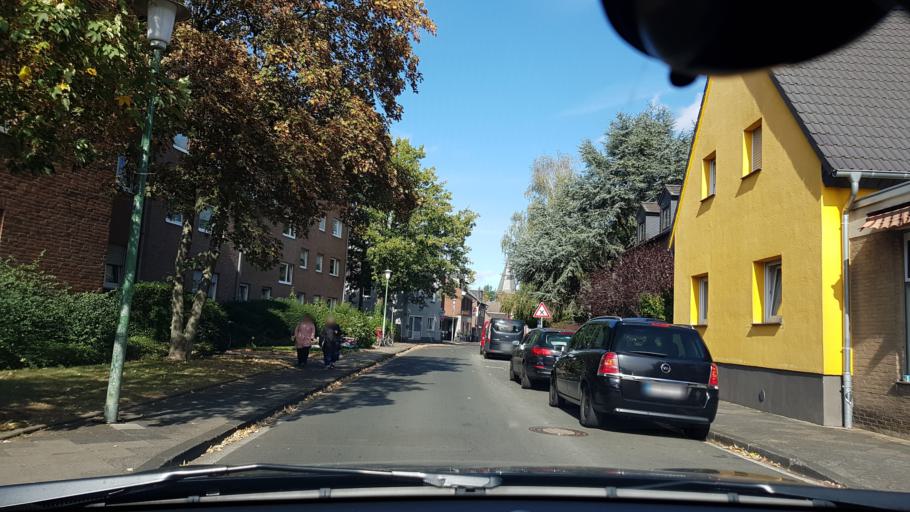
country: DE
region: North Rhine-Westphalia
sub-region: Regierungsbezirk Dusseldorf
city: Neuss
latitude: 51.1570
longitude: 6.6943
